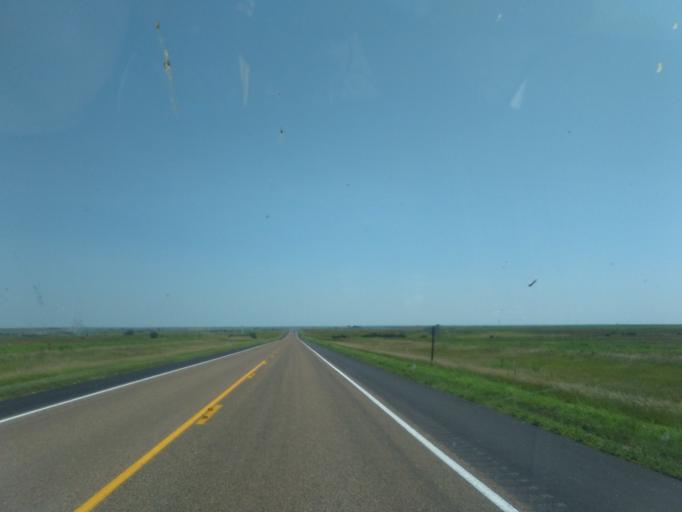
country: US
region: Nebraska
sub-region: Hitchcock County
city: Trenton
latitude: 40.2252
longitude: -100.9276
